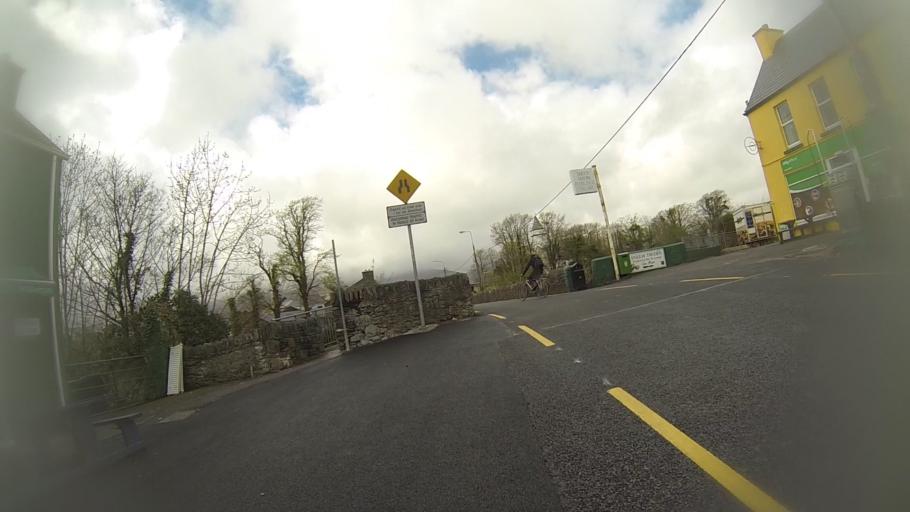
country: IE
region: Munster
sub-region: Ciarrai
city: Killorglin
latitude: 51.8380
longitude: -9.8993
